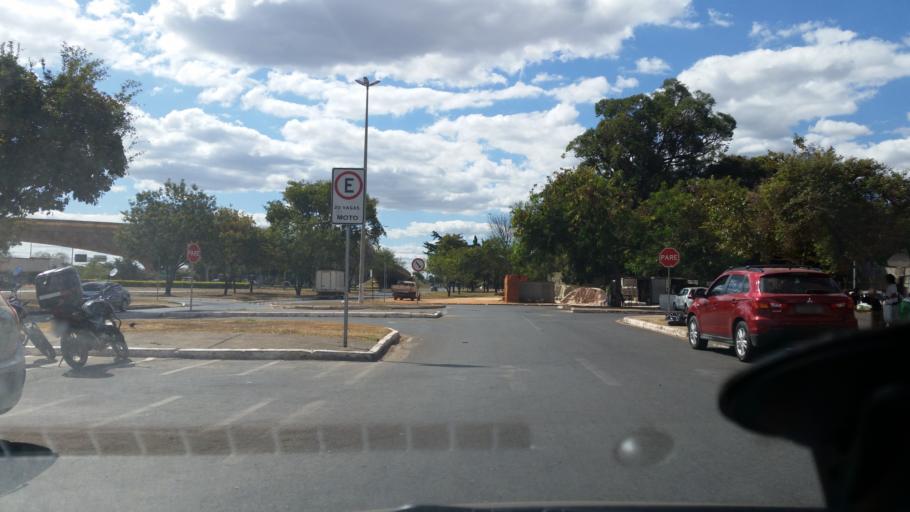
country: BR
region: Federal District
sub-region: Brasilia
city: Brasilia
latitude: -15.7871
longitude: -47.9409
